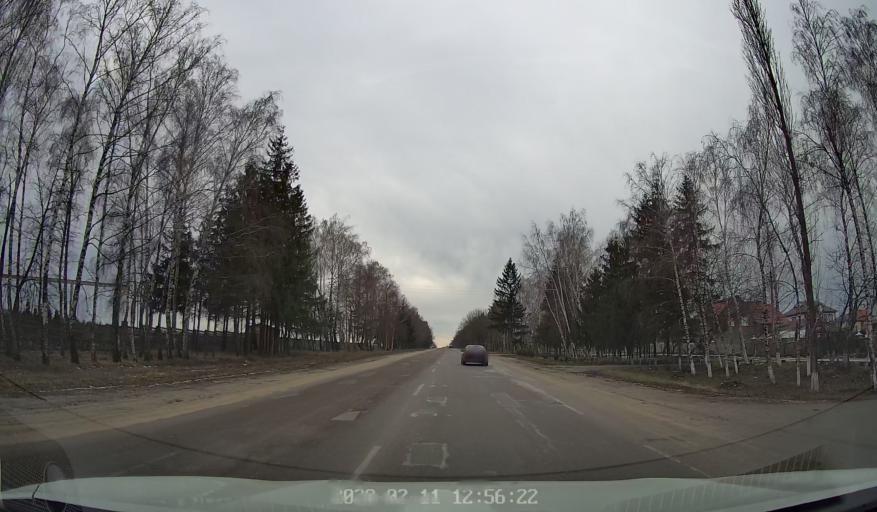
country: MD
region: Briceni
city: Briceni
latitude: 48.3498
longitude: 27.0814
